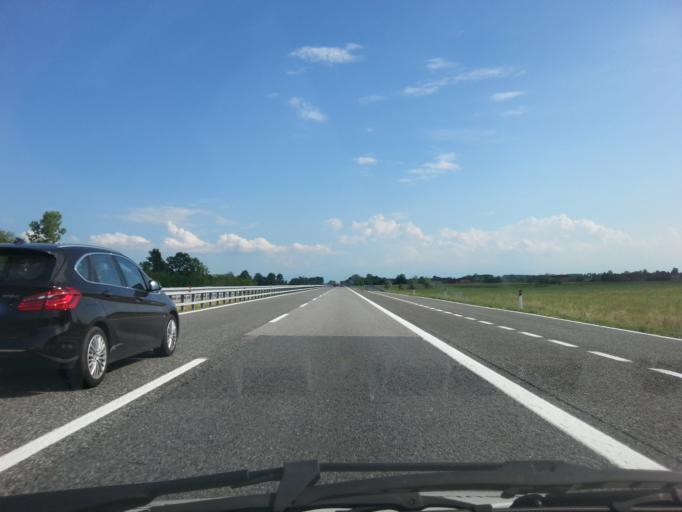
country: IT
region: Piedmont
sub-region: Provincia di Cuneo
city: Sanfre
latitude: 44.7186
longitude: 7.7588
